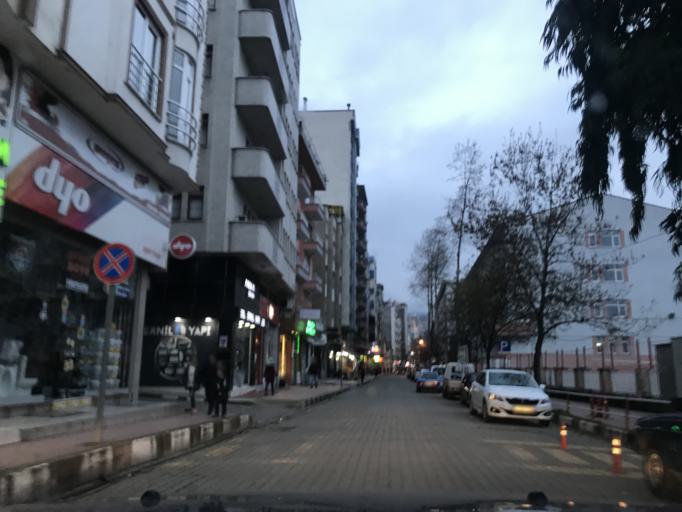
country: TR
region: Trabzon
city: Akcaabat
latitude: 41.0211
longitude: 39.5750
